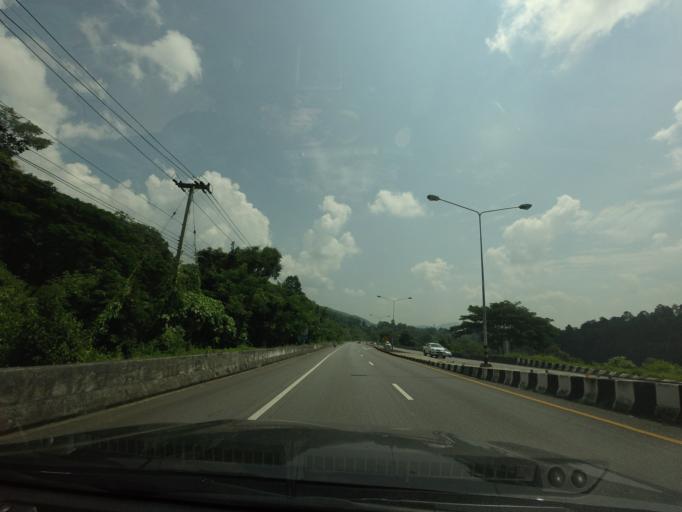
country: TH
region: Uttaradit
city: Lap Lae
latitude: 17.7770
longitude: 100.1262
